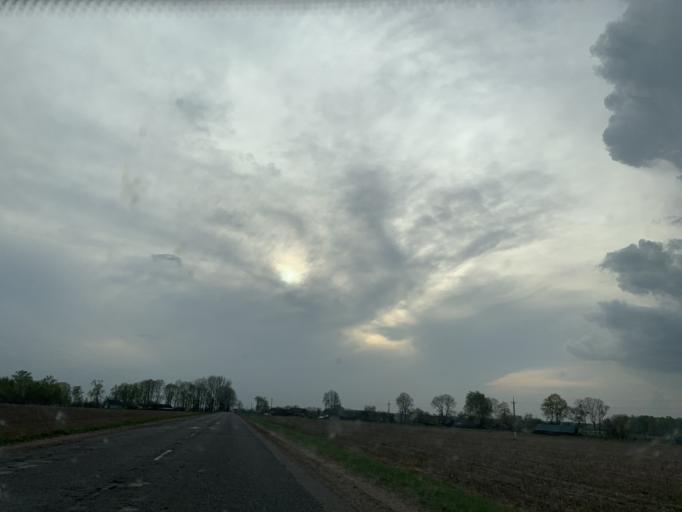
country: BY
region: Minsk
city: Kapyl'
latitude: 53.2904
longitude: 27.0130
